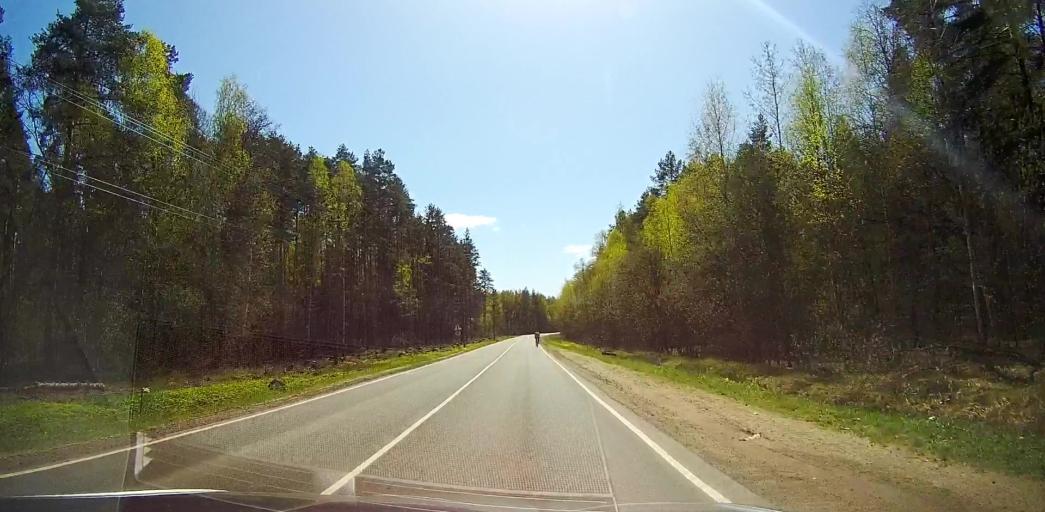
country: RU
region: Moskovskaya
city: Beloozerskiy
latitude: 55.5002
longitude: 38.4311
